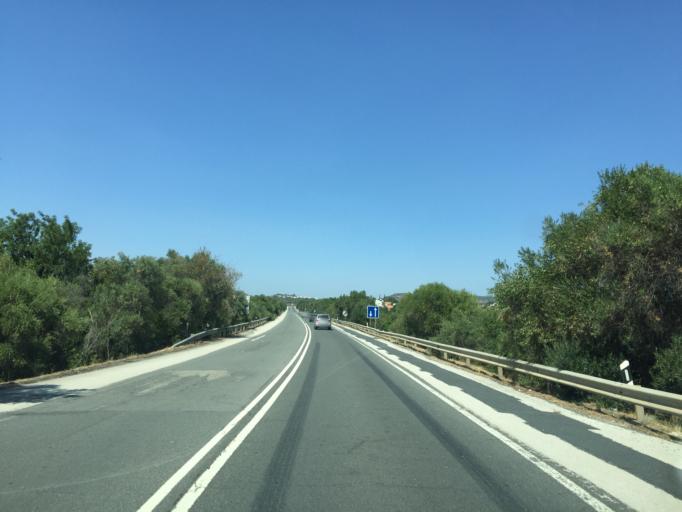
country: PT
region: Faro
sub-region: Silves
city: Sao Bartolomeu de Messines
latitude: 37.2082
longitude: -8.2574
